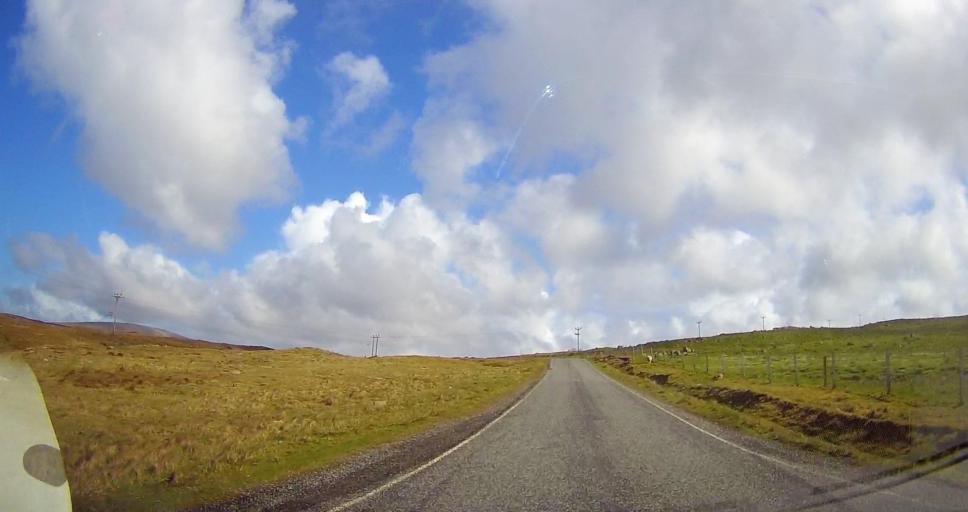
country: GB
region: Scotland
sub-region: Shetland Islands
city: Lerwick
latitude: 60.4799
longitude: -1.4060
